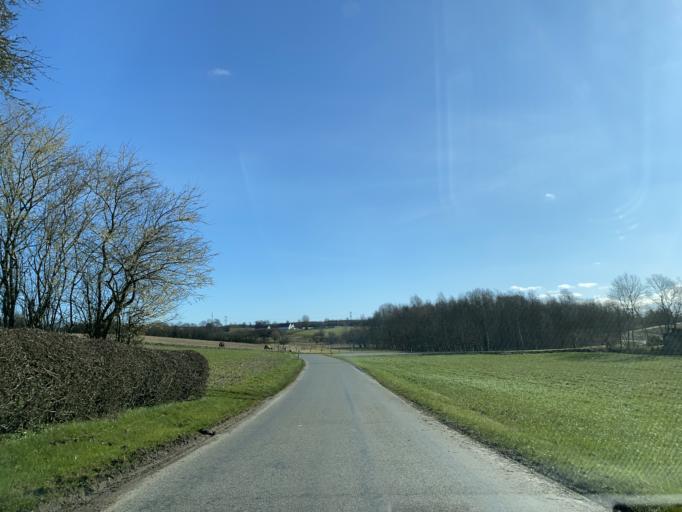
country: DK
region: Central Jutland
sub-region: Arhus Kommune
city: Sabro
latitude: 56.1799
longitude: 10.0386
